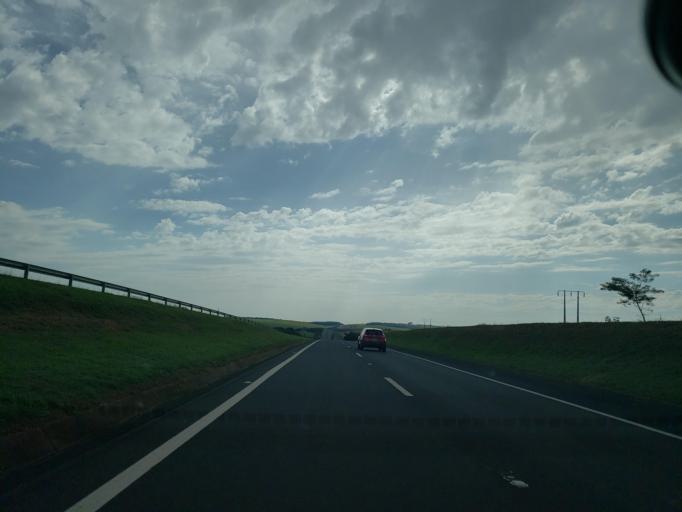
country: BR
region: Sao Paulo
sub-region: Lins
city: Lins
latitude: -21.7501
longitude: -49.6868
